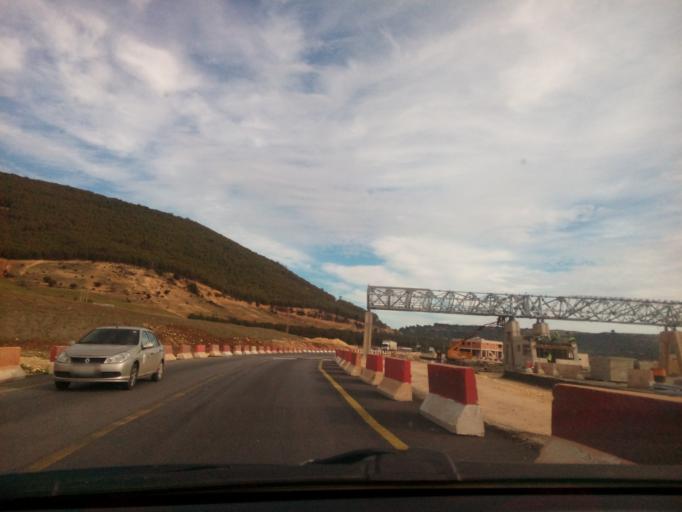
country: DZ
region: Sidi Bel Abbes
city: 'Ain el Berd
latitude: 35.3833
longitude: -0.4970
